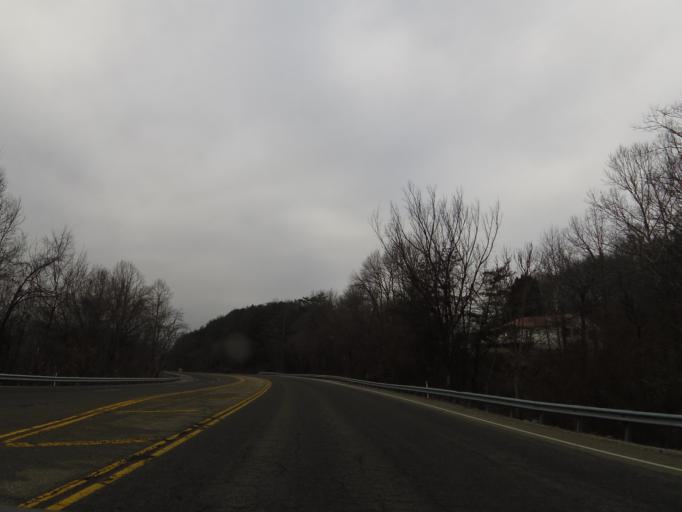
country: US
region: Tennessee
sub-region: Morgan County
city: Wartburg
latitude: 36.1086
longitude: -84.5971
